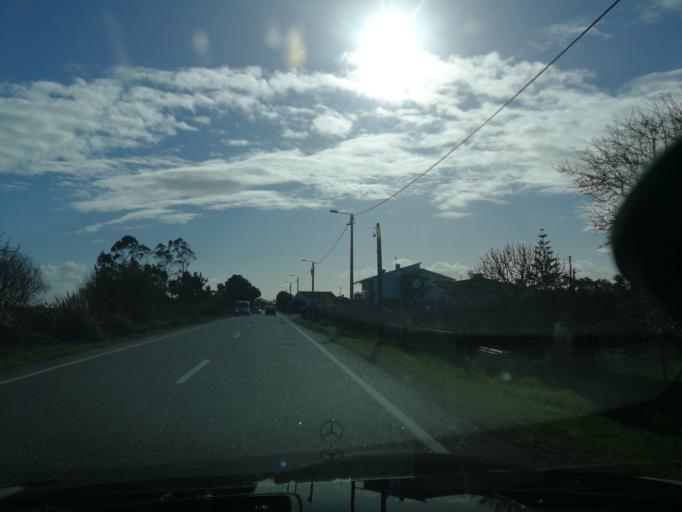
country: PT
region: Aveiro
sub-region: Estarreja
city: Pardilho
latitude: 40.8253
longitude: -8.6670
